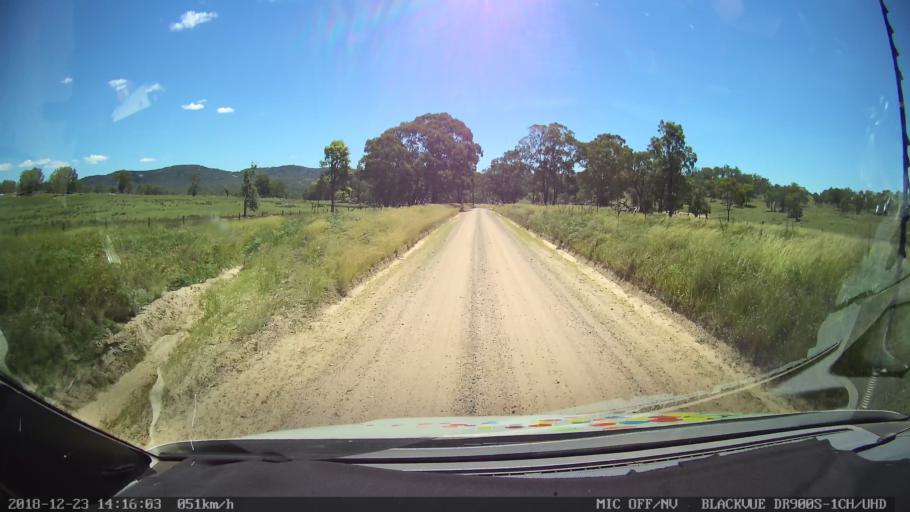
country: AU
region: New South Wales
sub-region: Tamworth Municipality
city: Manilla
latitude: -30.6605
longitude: 151.0214
